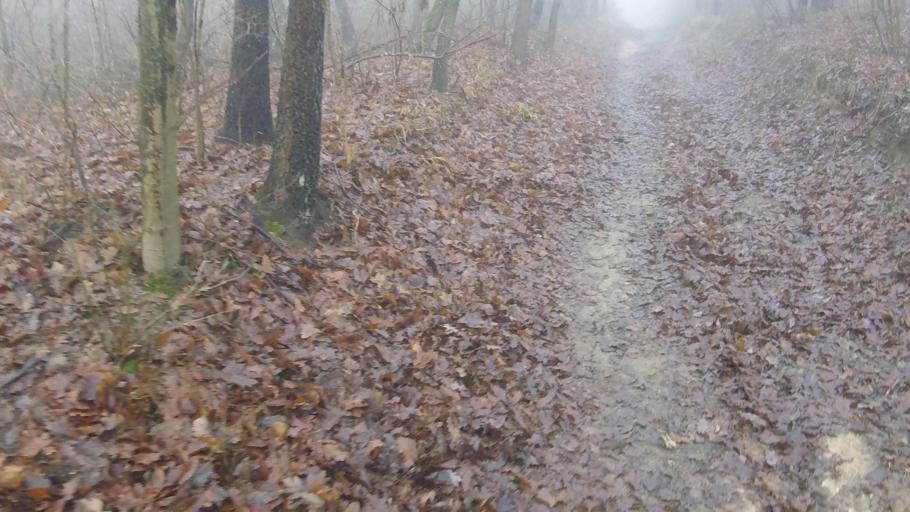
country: HU
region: Pest
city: Budakeszi
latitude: 47.5295
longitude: 18.9329
